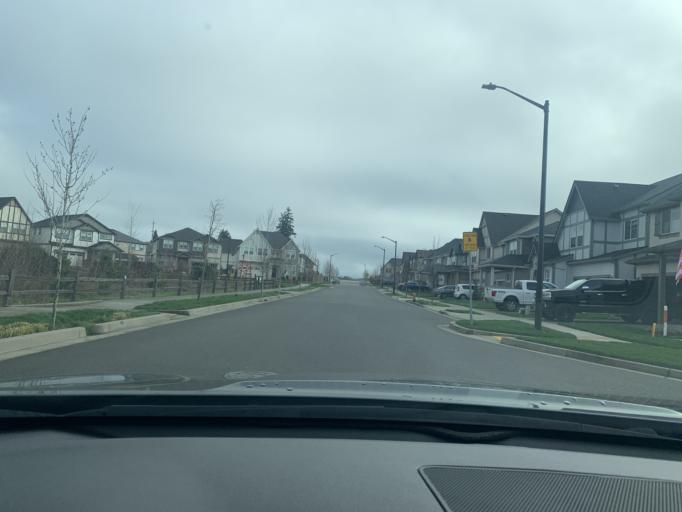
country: US
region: Oregon
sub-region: Washington County
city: North Plains
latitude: 45.5943
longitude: -122.9722
